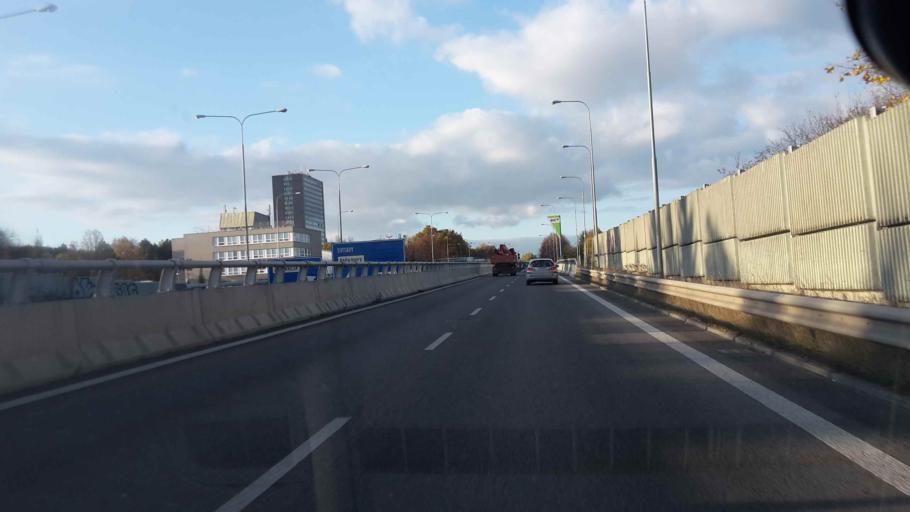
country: CZ
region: South Moravian
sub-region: Mesto Brno
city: Brno
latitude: 49.2200
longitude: 16.5832
